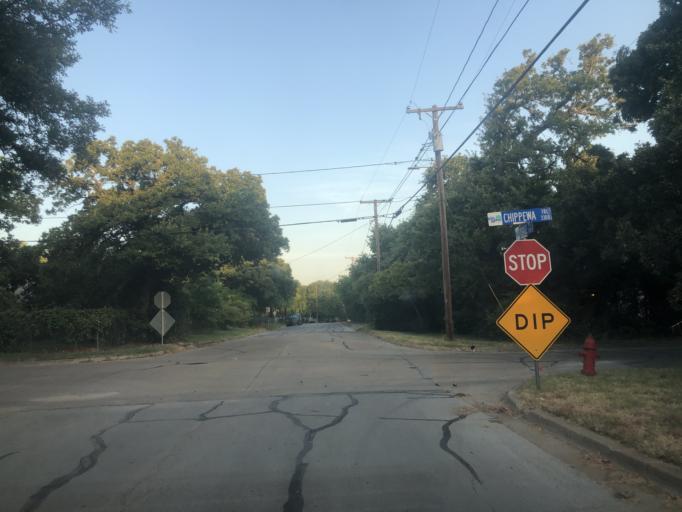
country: US
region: Texas
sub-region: Tarrant County
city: Lake Worth
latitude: 32.8050
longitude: -97.4494
